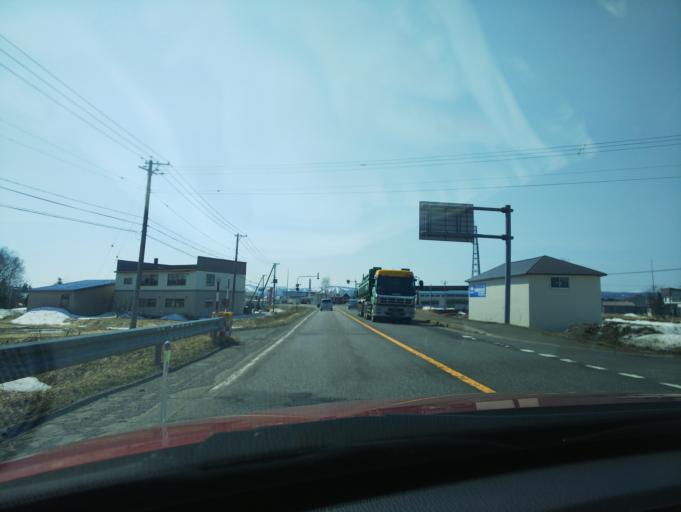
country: JP
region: Hokkaido
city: Nayoro
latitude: 44.2980
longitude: 142.4270
